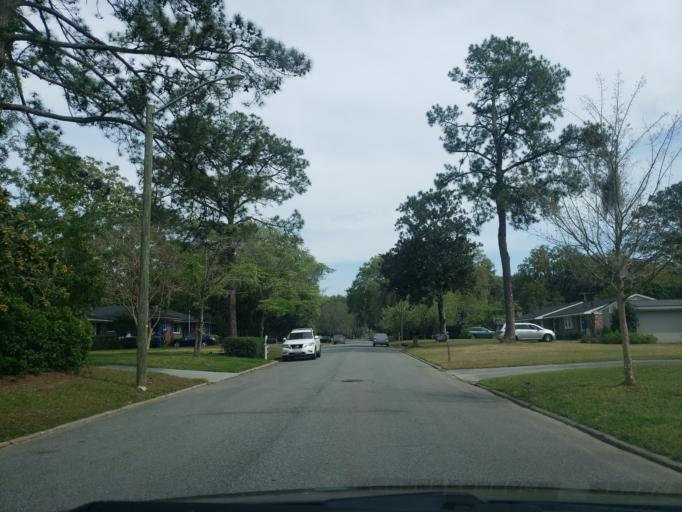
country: US
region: Georgia
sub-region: Chatham County
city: Isle of Hope
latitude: 31.9934
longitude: -81.0983
